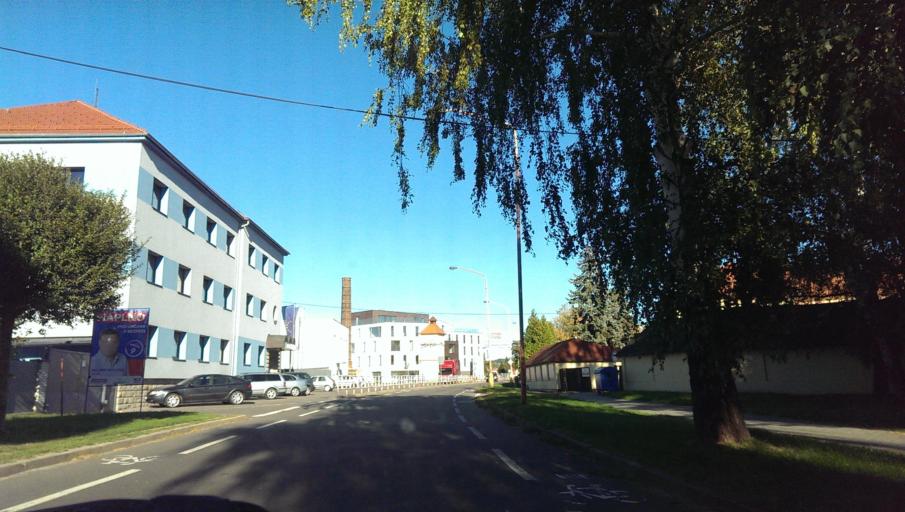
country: CZ
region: Zlin
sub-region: Okres Uherske Hradiste
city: Uherske Hradiste
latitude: 49.0721
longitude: 17.4535
